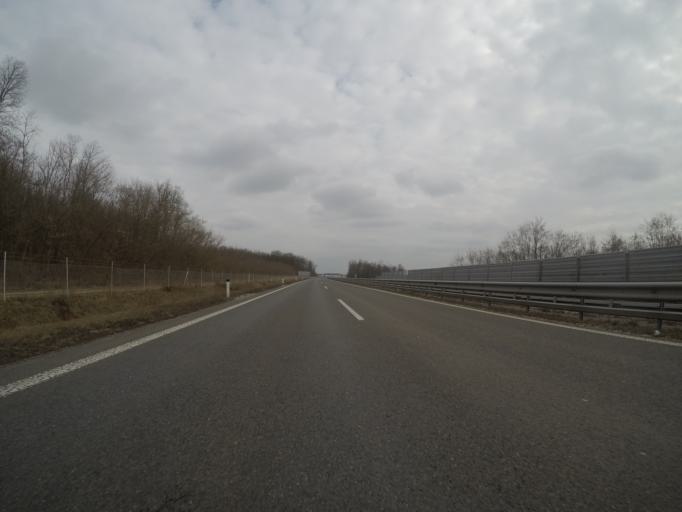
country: SI
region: Beltinci
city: Gancani
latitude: 46.6365
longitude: 16.2701
